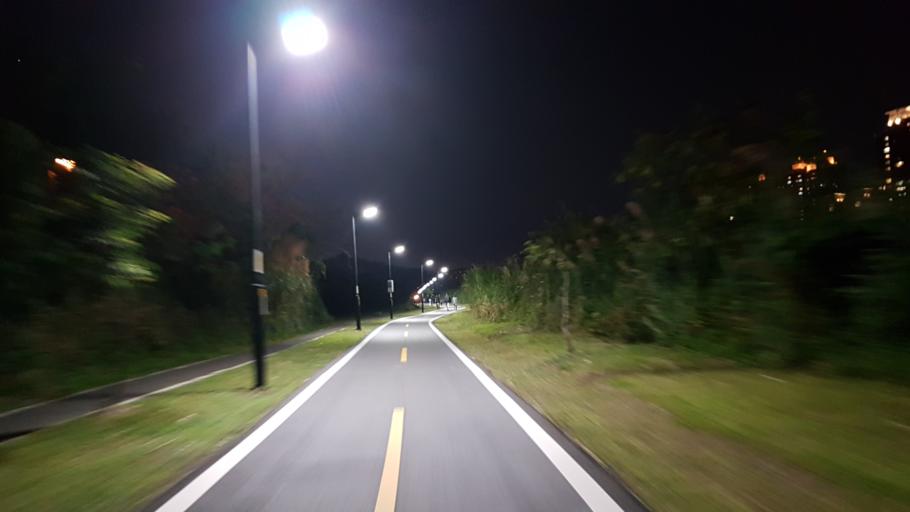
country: TW
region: Taipei
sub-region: Taipei
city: Banqiao
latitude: 24.9717
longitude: 121.5256
